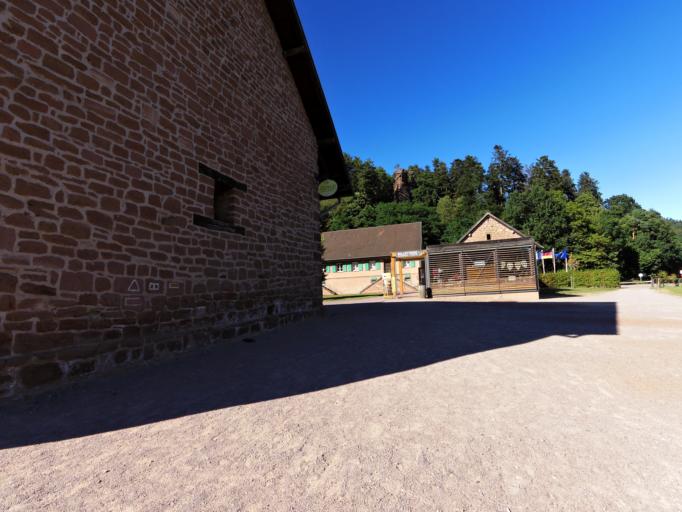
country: DE
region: Rheinland-Pfalz
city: Hirschthal
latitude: 49.0467
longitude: 7.7744
